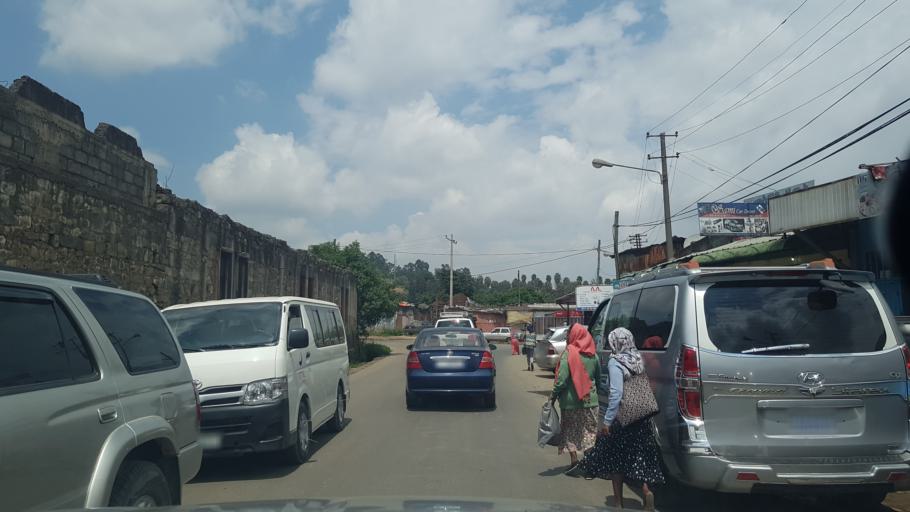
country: ET
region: Adis Abeba
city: Addis Ababa
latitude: 9.0217
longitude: 38.7552
